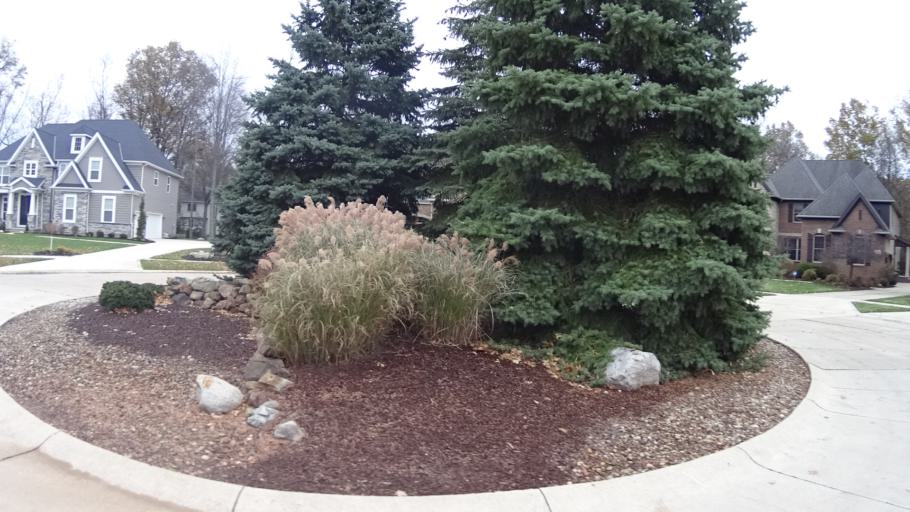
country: US
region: Ohio
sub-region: Lorain County
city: Avon Lake
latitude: 41.4916
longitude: -81.9991
